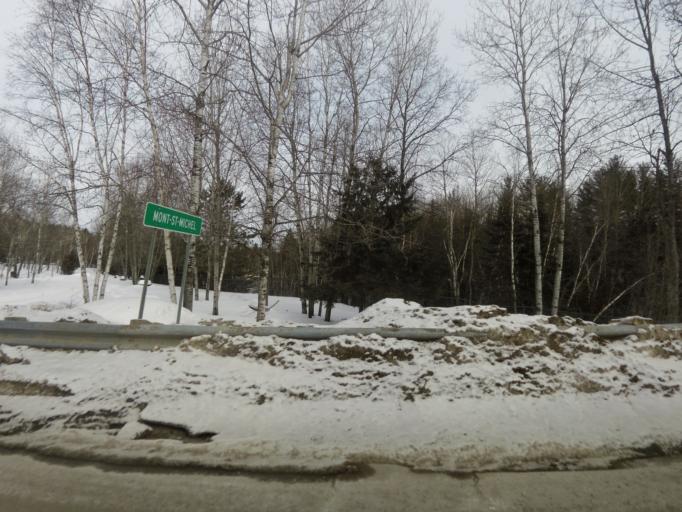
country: CA
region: Quebec
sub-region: Laurentides
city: Ferme-Neuve
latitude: 46.7760
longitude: -75.3365
